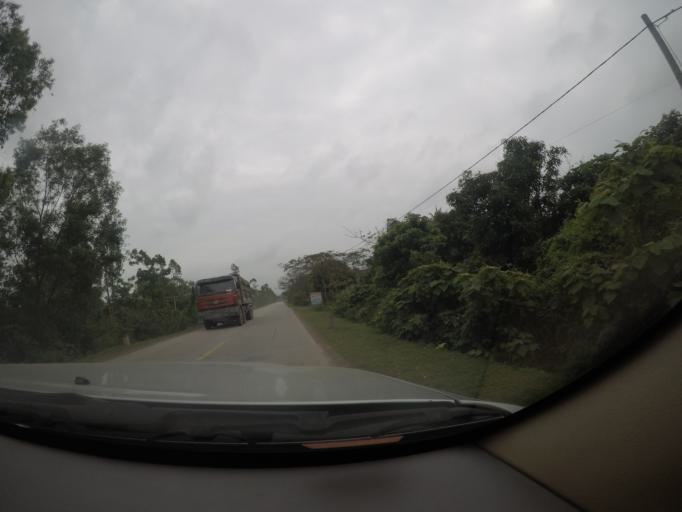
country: VN
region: Quang Binh
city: Quan Hau
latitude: 17.2926
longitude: 106.6444
